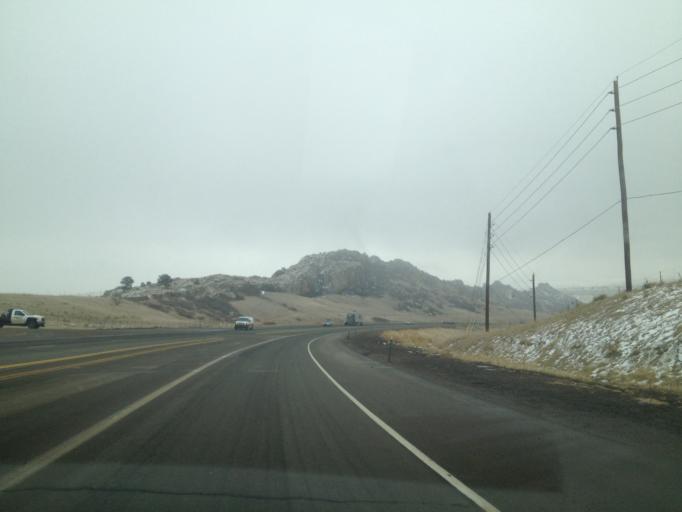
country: US
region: Colorado
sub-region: Jefferson County
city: Golden
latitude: 39.8574
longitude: -105.2333
